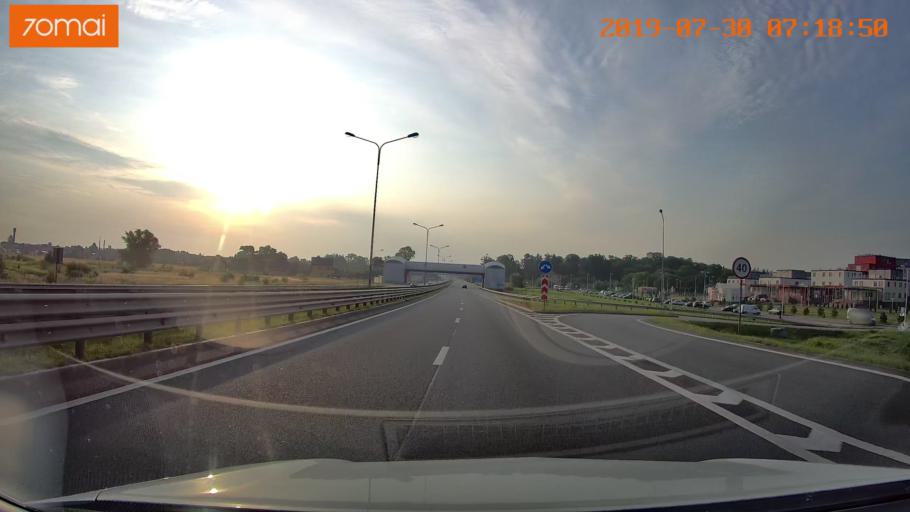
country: RU
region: Kaliningrad
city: Bol'shoe Isakovo
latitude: 54.7024
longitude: 20.6582
